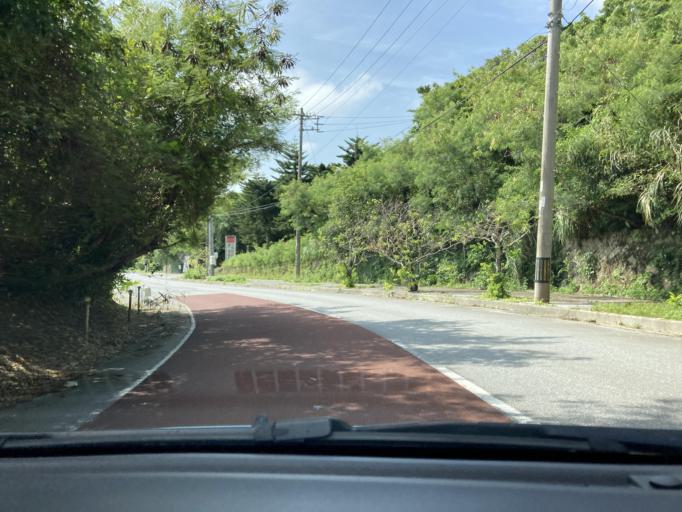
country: JP
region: Okinawa
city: Chatan
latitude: 26.2815
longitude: 127.7989
